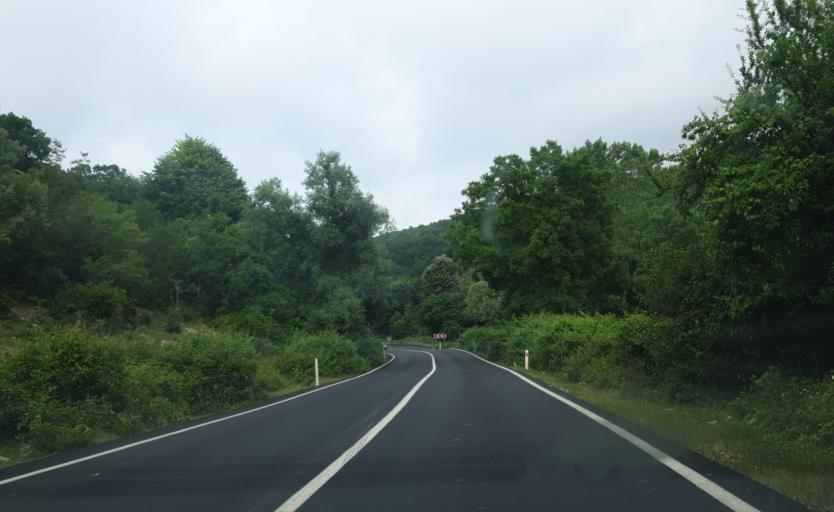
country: TR
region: Kirklareli
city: Salmydessus
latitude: 41.6100
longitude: 28.0861
